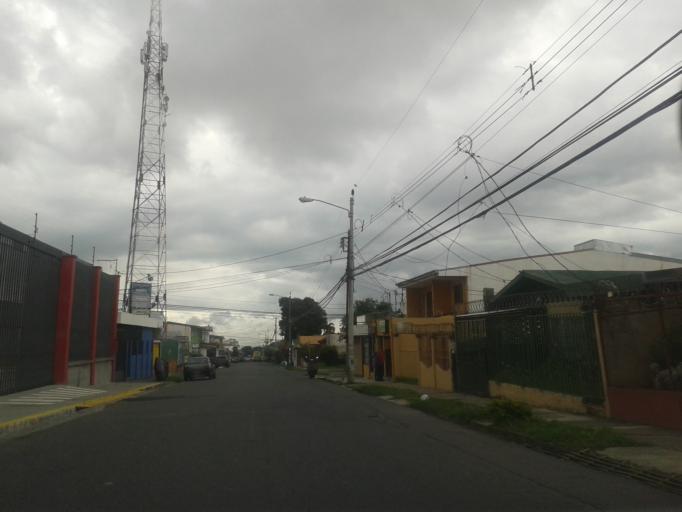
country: CR
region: San Jose
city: San Juan
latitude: 9.9632
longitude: -84.0785
